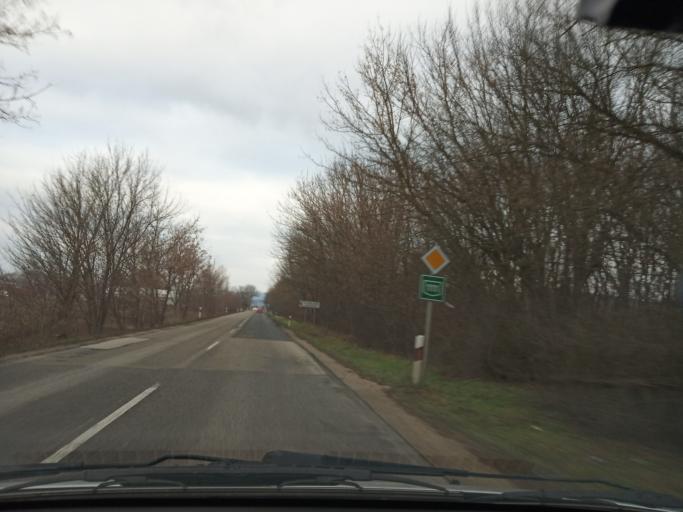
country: HU
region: Komarom-Esztergom
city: Esztergom
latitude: 47.7595
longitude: 18.7355
